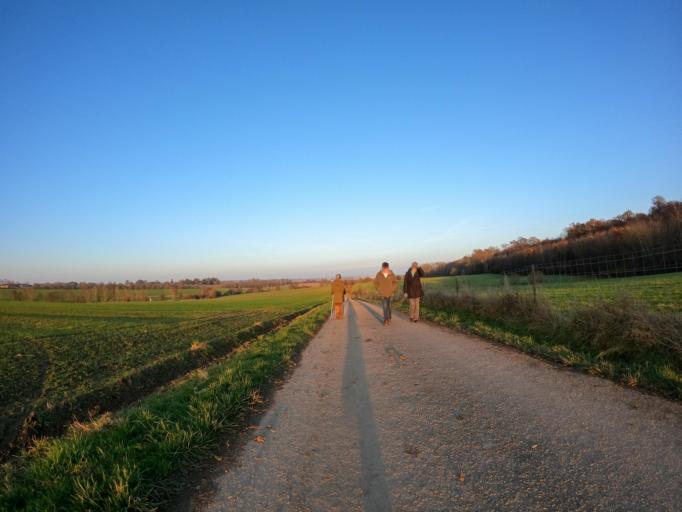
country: LU
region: Luxembourg
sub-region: Canton de Luxembourg
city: Bertrange
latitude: 49.5898
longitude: 6.0374
